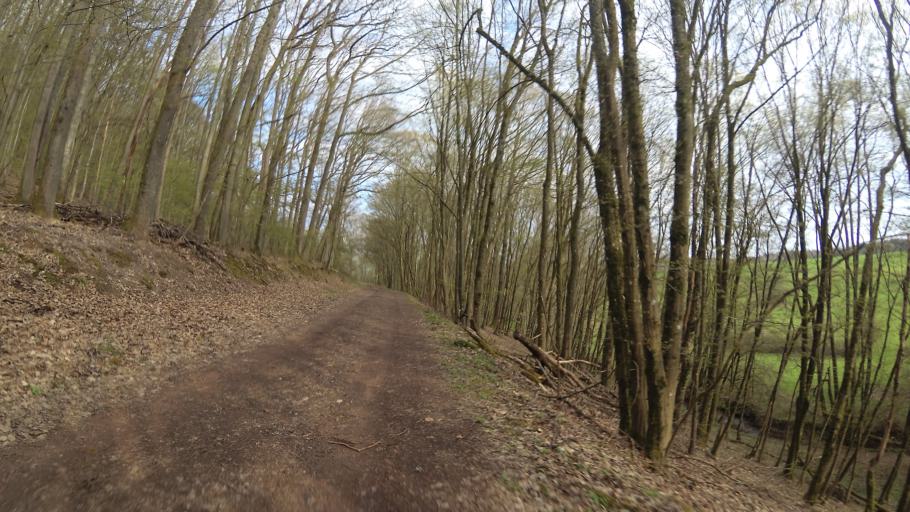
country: DE
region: Saarland
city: Sankt Wendel
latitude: 49.4571
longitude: 7.2144
